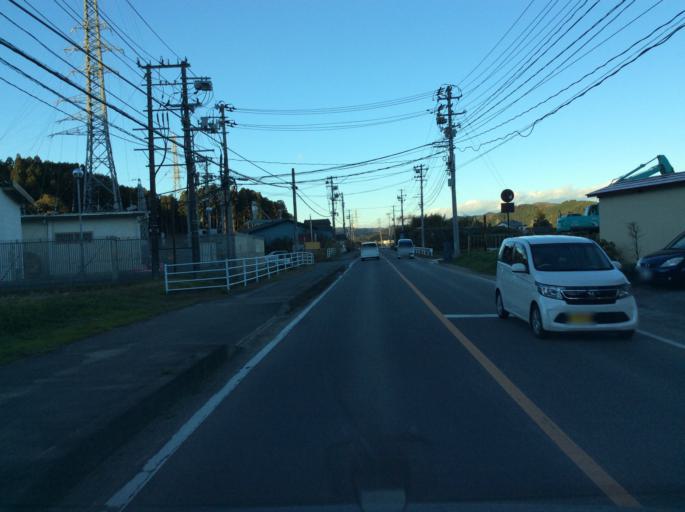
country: JP
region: Fukushima
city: Iwaki
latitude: 37.0659
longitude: 140.8702
